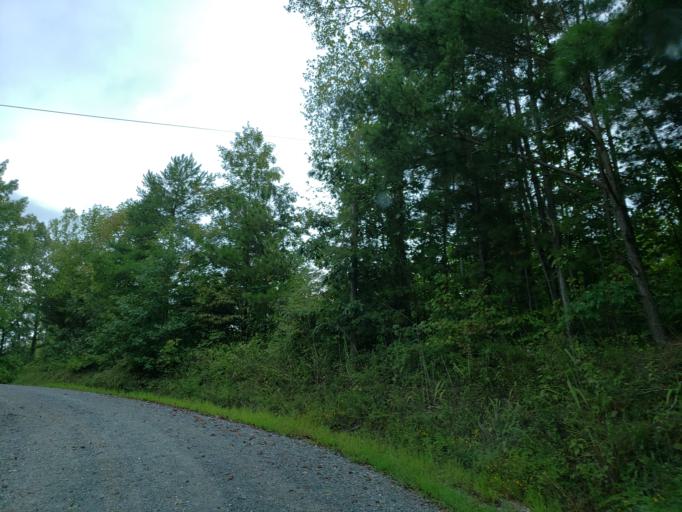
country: US
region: Georgia
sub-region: Pickens County
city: Jasper
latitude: 34.5526
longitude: -84.5142
